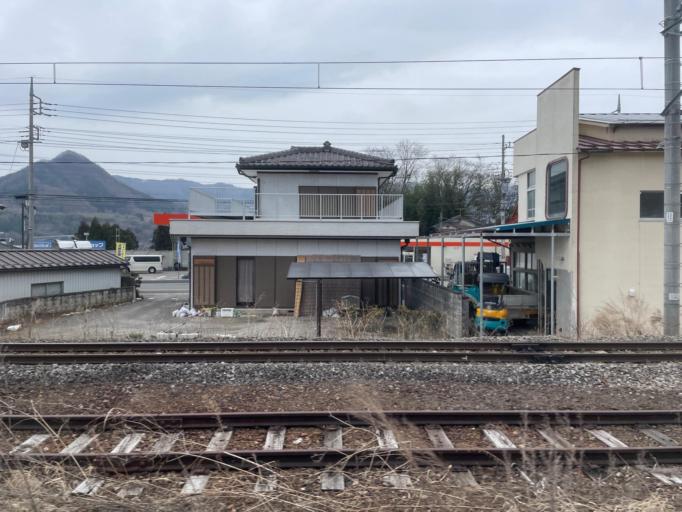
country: JP
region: Gunma
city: Numata
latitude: 36.6784
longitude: 139.0017
